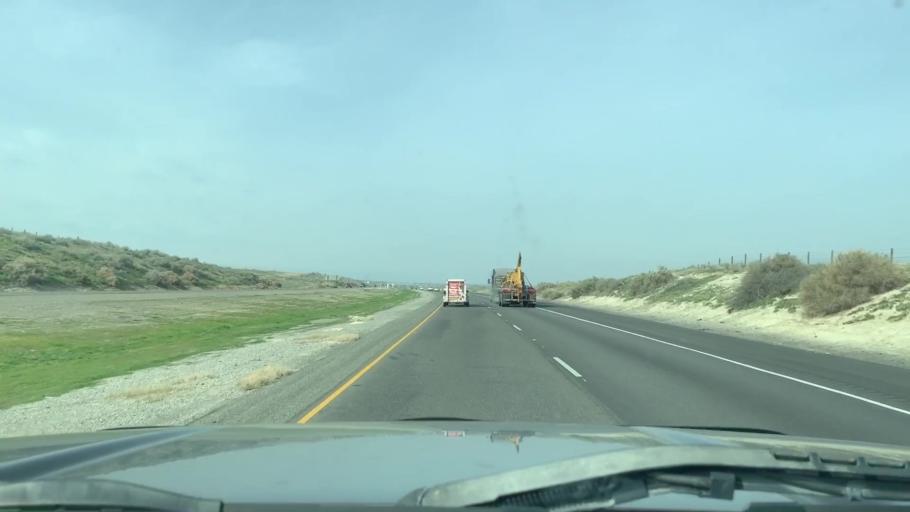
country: US
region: California
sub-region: Fresno County
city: Mendota
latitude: 36.5203
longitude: -120.4740
